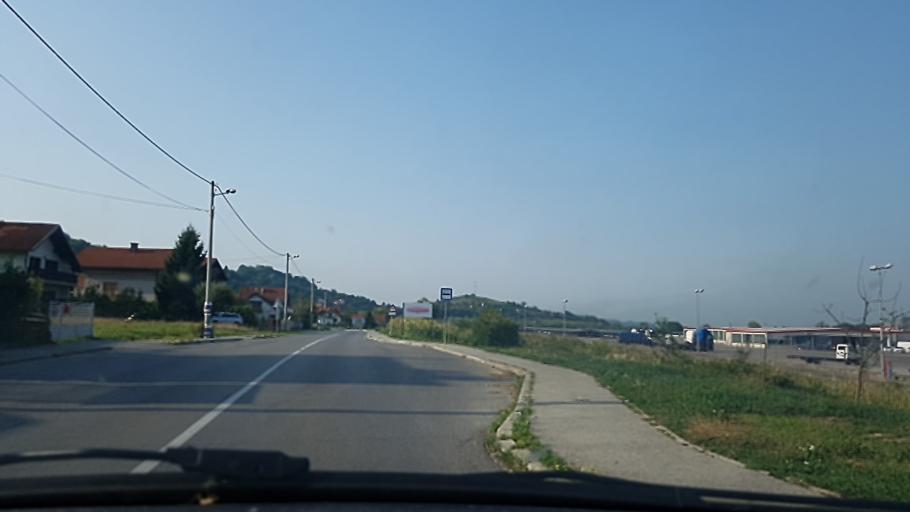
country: HR
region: Zagrebacka
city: Pojatno
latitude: 45.9126
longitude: 15.8084
